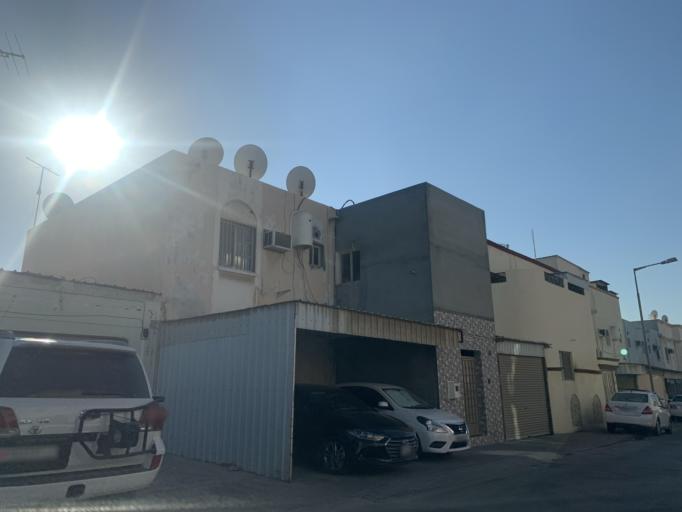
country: BH
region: Central Governorate
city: Madinat Hamad
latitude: 26.1105
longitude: 50.5081
